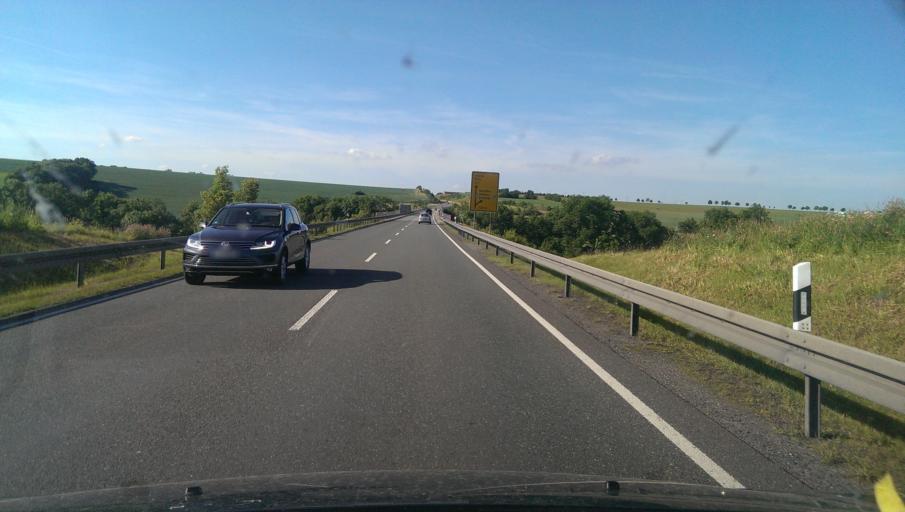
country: DE
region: Thuringia
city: Schwaara
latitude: 50.9147
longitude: 12.1336
